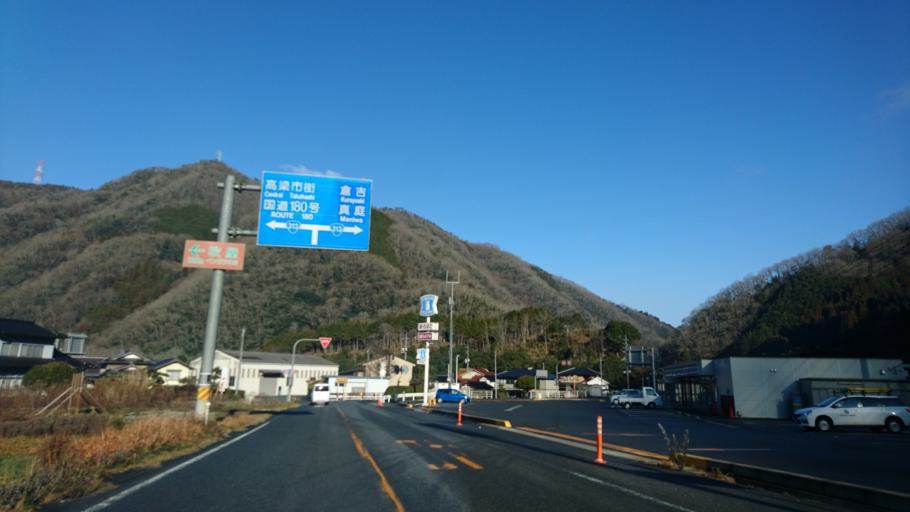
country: JP
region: Okayama
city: Takahashi
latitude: 34.8293
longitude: 133.6311
